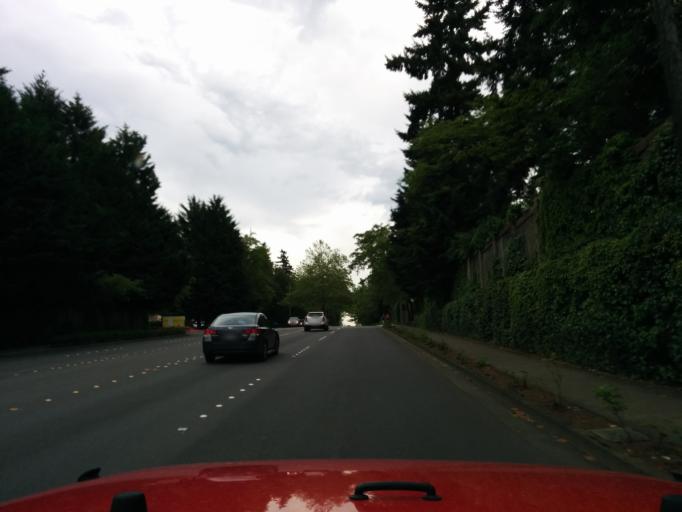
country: US
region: Washington
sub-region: King County
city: Eastgate
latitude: 47.6169
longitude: -122.1373
